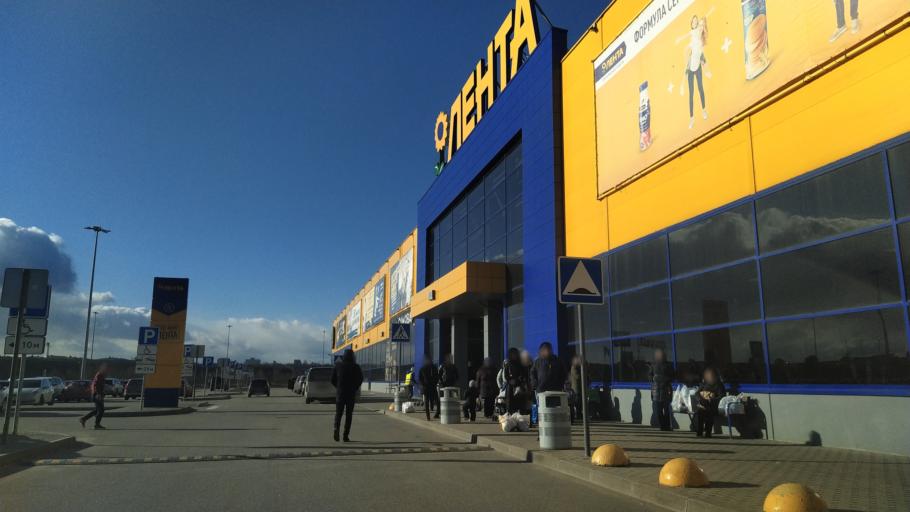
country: RU
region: Leningrad
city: Bugry
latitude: 60.0607
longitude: 30.3932
